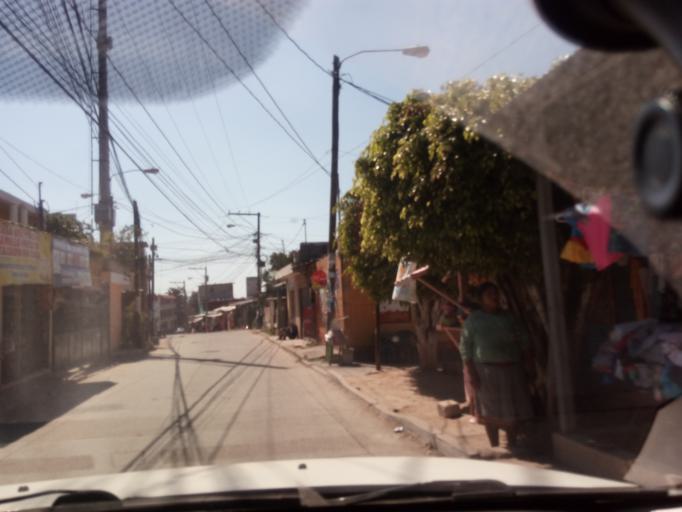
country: GT
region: Guatemala
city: Mixco
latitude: 14.6178
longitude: -90.5848
